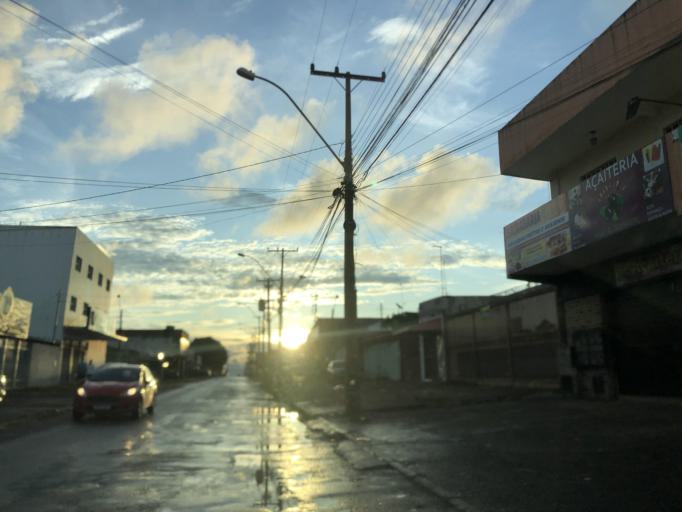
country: BR
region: Federal District
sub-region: Brasilia
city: Brasilia
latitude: -15.8277
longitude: -48.0996
